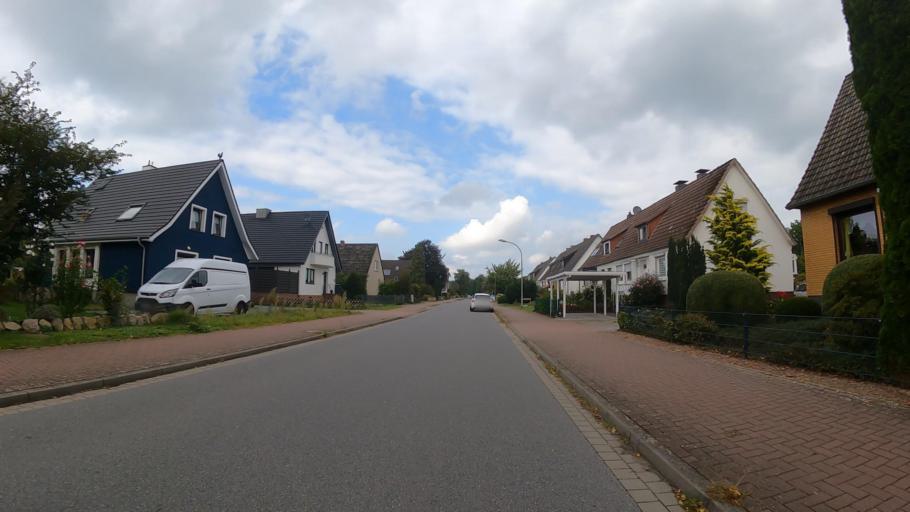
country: DE
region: Schleswig-Holstein
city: Tornesch
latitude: 53.7049
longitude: 9.7139
